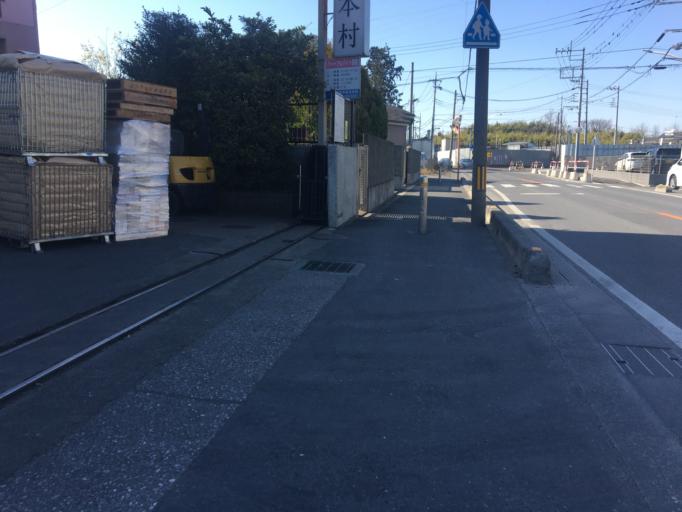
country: JP
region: Saitama
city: Shiki
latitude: 35.8301
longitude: 139.6066
